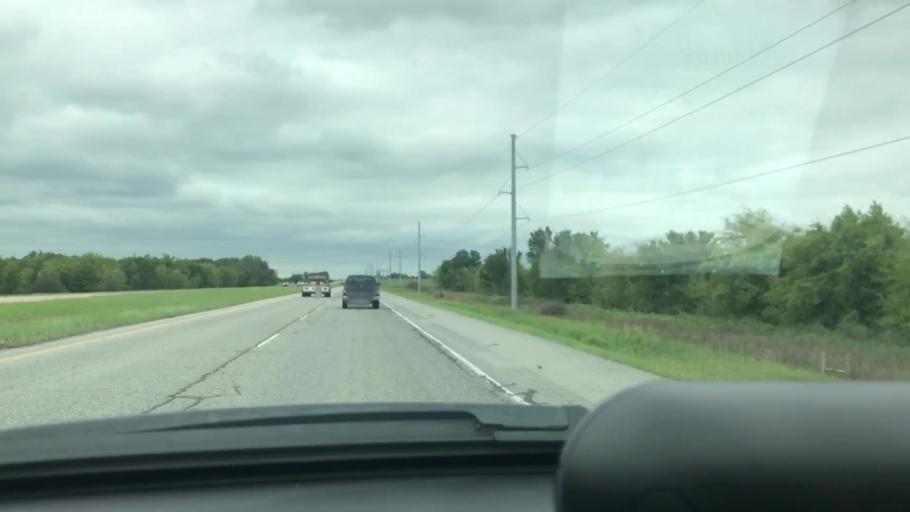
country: US
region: Oklahoma
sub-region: Wagoner County
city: Wagoner
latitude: 36.0027
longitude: -95.3685
